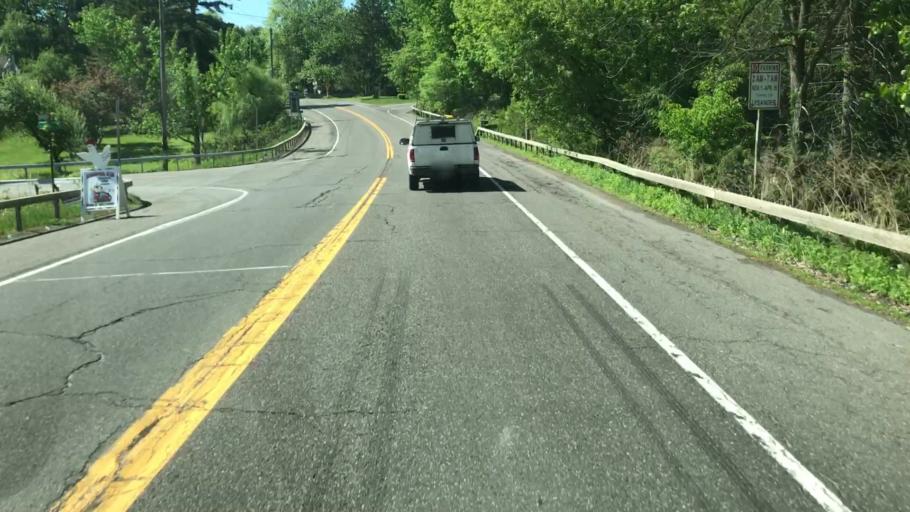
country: US
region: New York
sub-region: Onondaga County
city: Seneca Knolls
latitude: 43.1312
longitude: -76.2542
